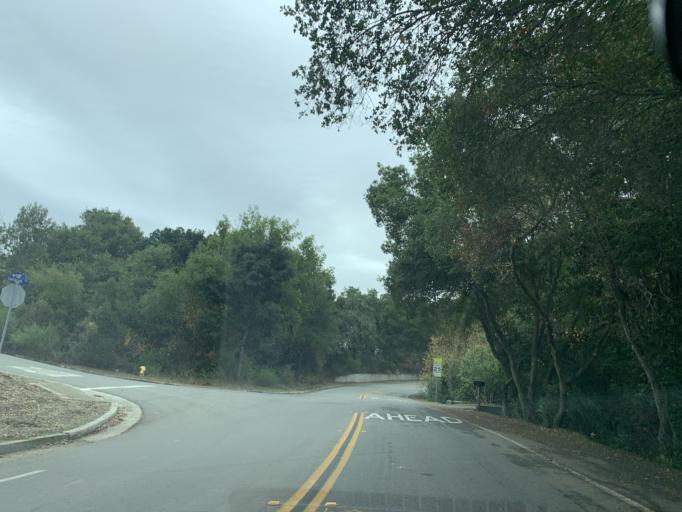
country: US
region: California
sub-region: Santa Clara County
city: Loyola
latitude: 37.3433
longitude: -122.0969
